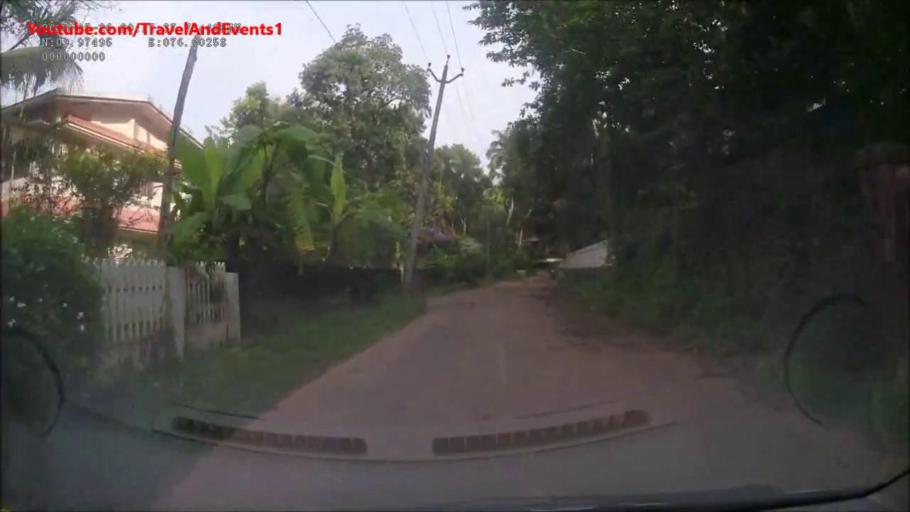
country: IN
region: Kerala
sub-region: Ernakulam
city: Muvattupula
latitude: 9.9690
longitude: 76.6096
